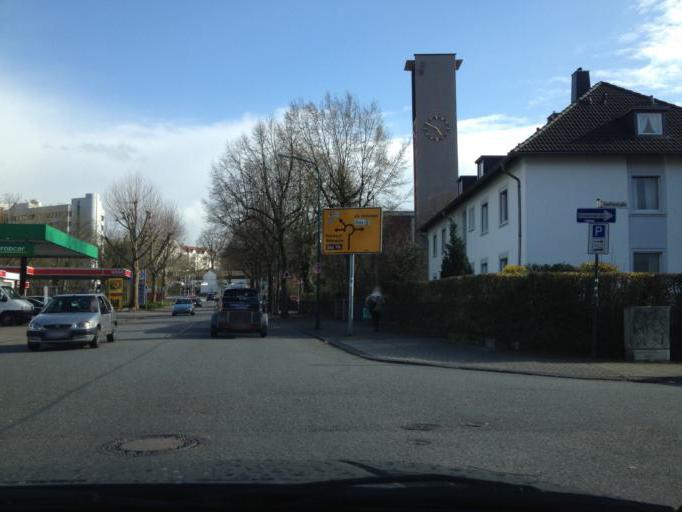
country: DE
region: Saarland
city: Neunkirchen
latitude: 49.3520
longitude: 7.1823
